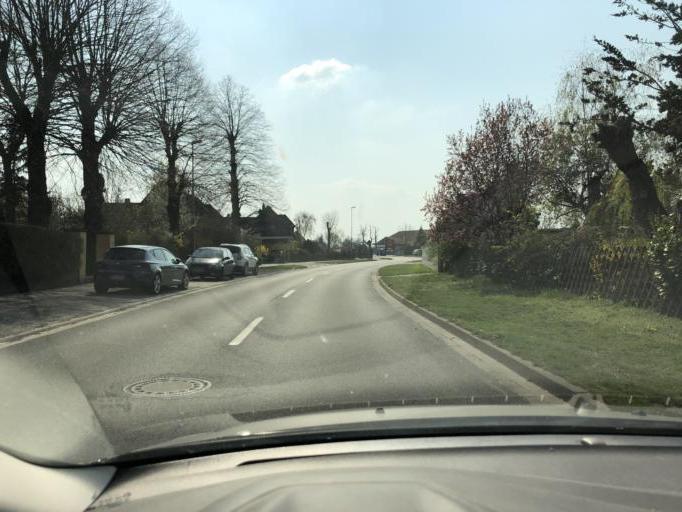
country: DE
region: Saxony-Anhalt
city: Hohenthurm
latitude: 51.5196
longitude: 12.0979
